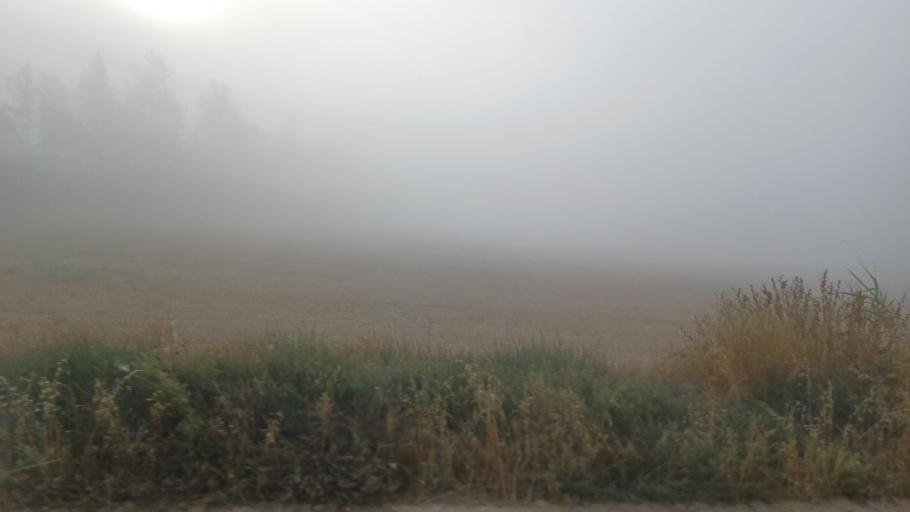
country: CY
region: Ammochostos
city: Acheritou
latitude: 35.0918
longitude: 33.8763
